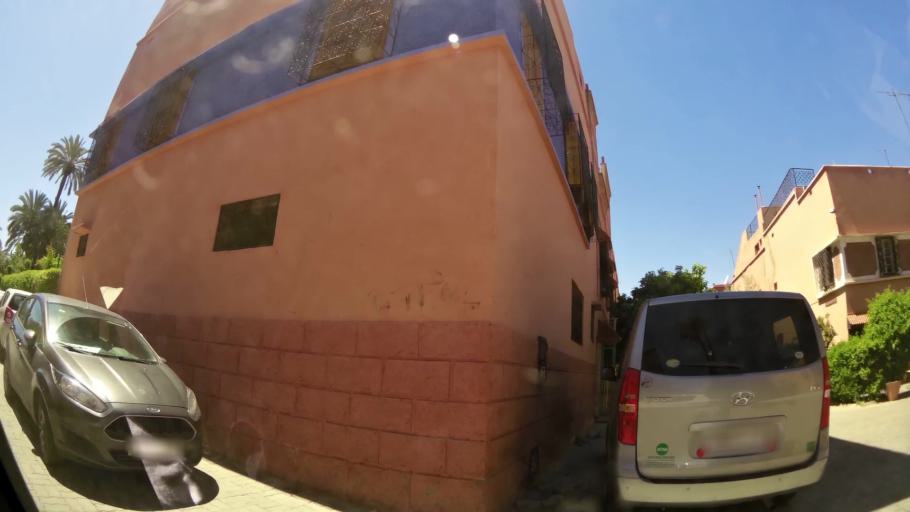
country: MA
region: Marrakech-Tensift-Al Haouz
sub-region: Marrakech
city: Marrakesh
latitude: 31.6468
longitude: -7.9918
